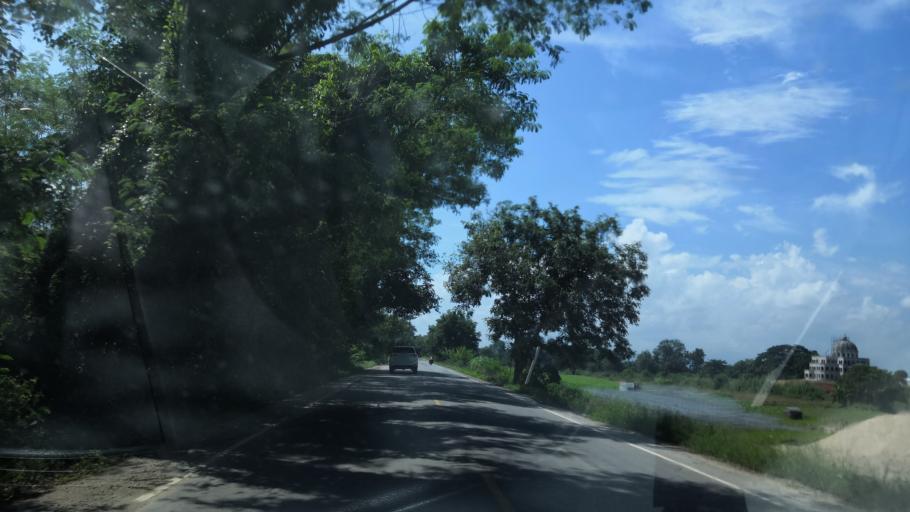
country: TH
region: Chiang Rai
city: Wiang Chai
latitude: 19.9562
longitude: 99.9398
